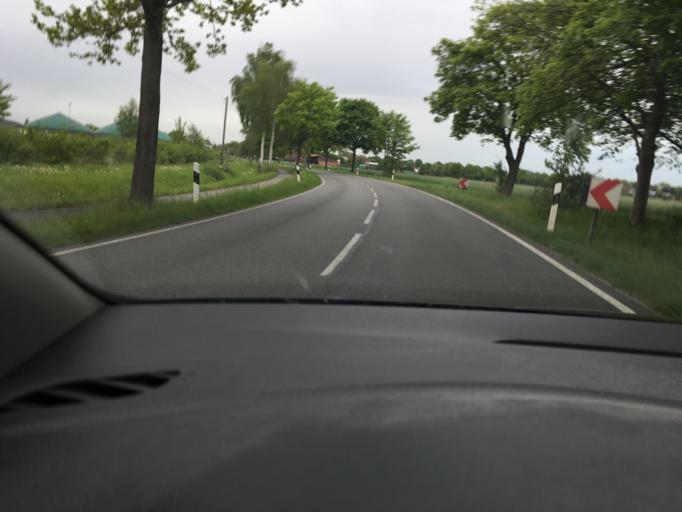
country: DE
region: Lower Saxony
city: Arpke
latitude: 52.3875
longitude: 10.0536
